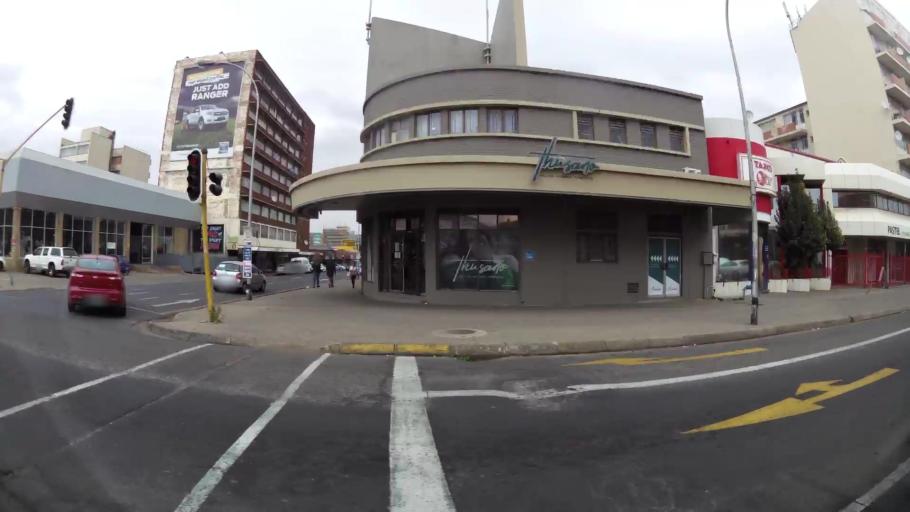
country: ZA
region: Orange Free State
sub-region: Mangaung Metropolitan Municipality
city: Bloemfontein
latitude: -29.1129
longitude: 26.2192
